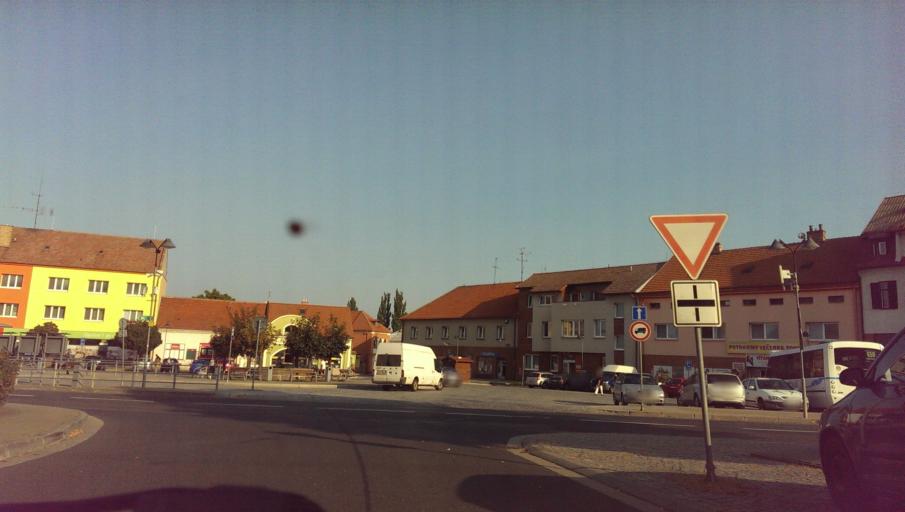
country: CZ
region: Zlin
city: Korycany
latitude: 49.1061
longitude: 17.1640
